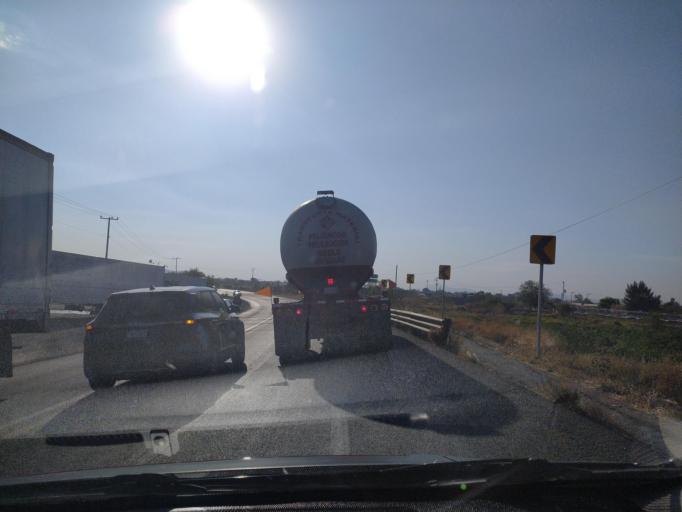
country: MX
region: Michoacan
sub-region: Yurecuaro
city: Yurecuaro
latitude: 20.3293
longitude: -102.2656
